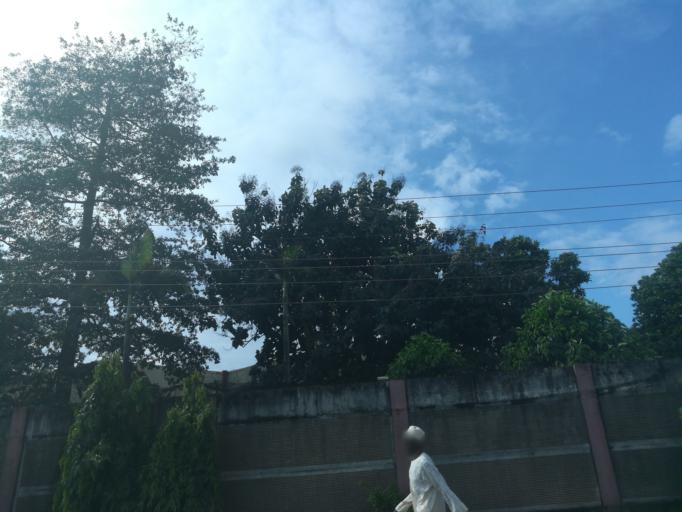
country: NG
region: Lagos
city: Agege
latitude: 6.6267
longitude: 3.3475
